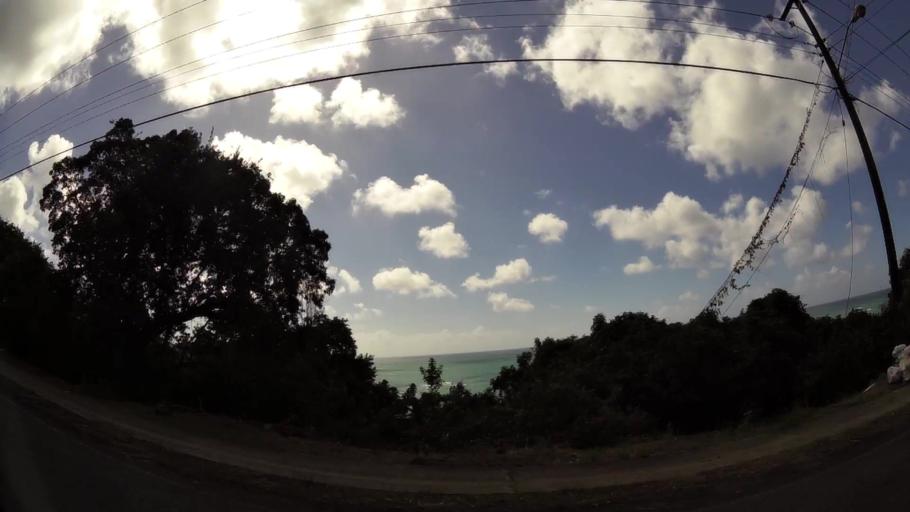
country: LC
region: Laborie Quarter
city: Laborie
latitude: 13.7537
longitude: -60.9990
